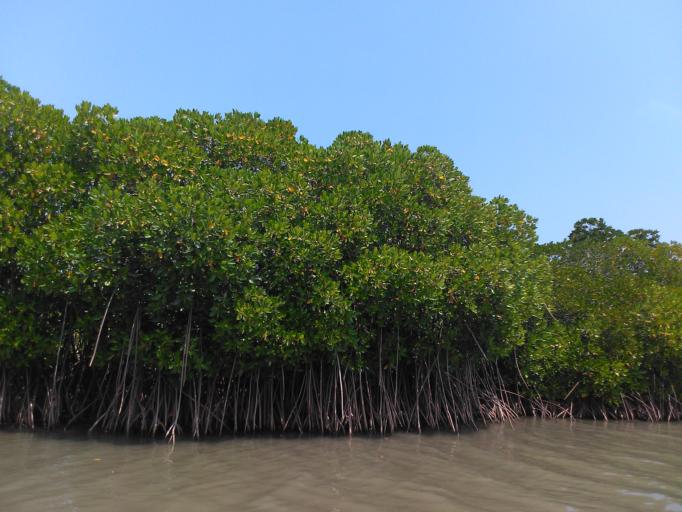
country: IN
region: Tamil Nadu
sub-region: Cuddalore
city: Annamalainagar
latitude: 11.4440
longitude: 79.7933
